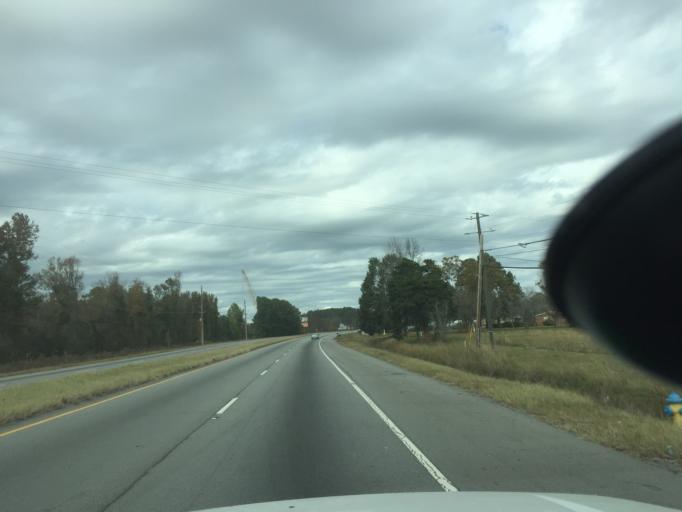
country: US
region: Georgia
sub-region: Chatham County
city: Port Wentworth
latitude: 32.1678
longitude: -81.1859
